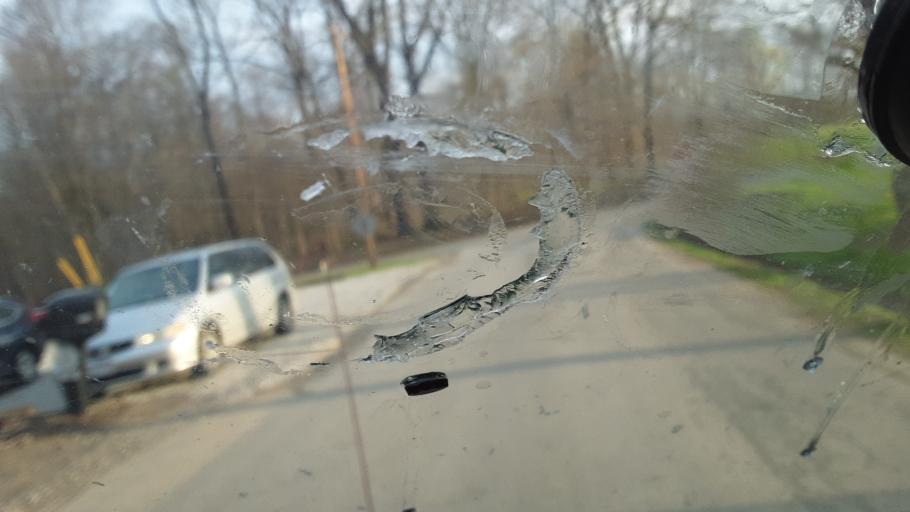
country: US
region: Ohio
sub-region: Richland County
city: Lincoln Heights
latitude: 40.7197
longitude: -82.4268
